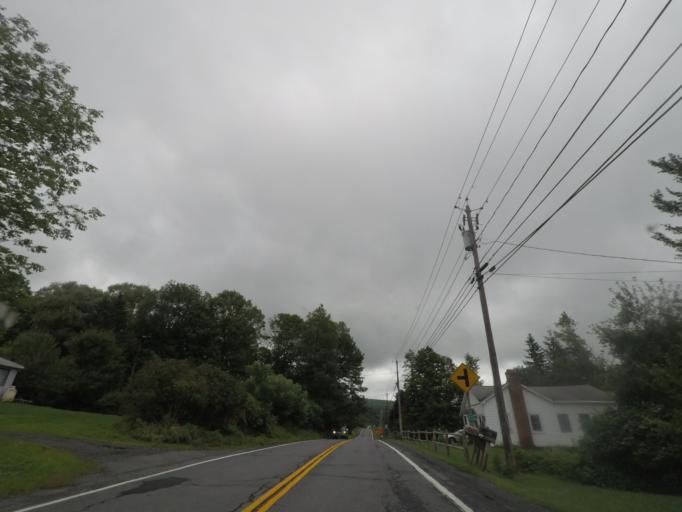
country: US
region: New York
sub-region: Rensselaer County
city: Averill Park
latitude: 42.5880
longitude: -73.4906
